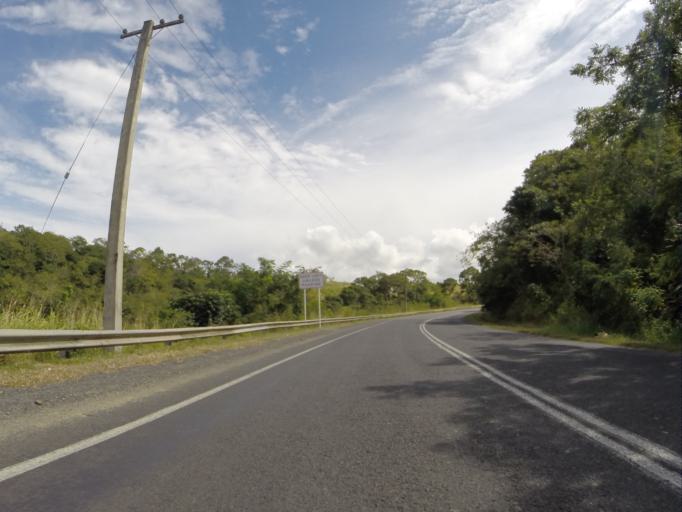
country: FJ
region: Western
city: Nadi
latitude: -18.1217
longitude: 177.4127
